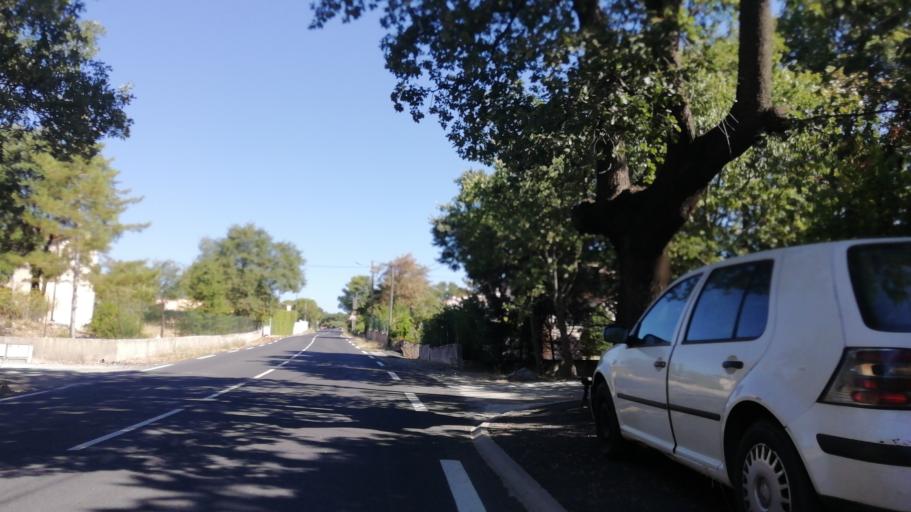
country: FR
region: Languedoc-Roussillon
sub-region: Departement de l'Herault
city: Saint-Martin-de-Londres
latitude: 43.7930
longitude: 3.7303
